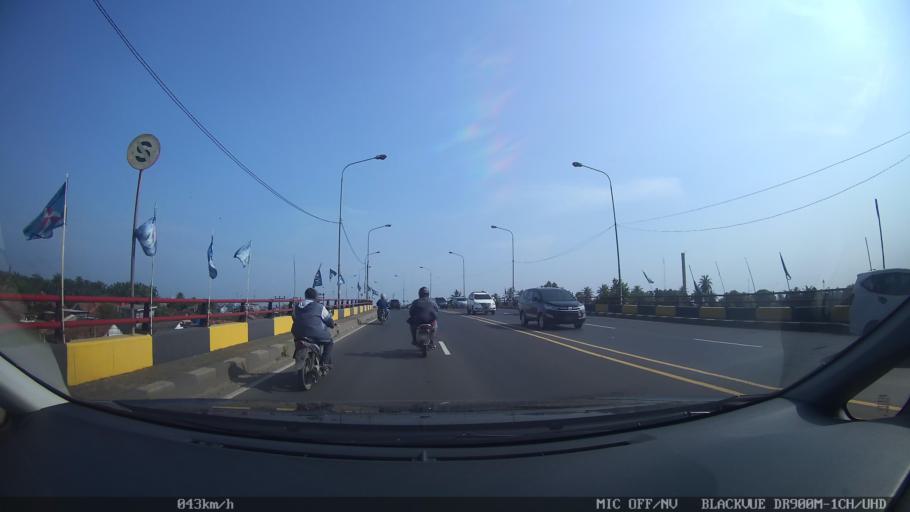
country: ID
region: Lampung
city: Natar
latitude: -5.3224
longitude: 105.2013
